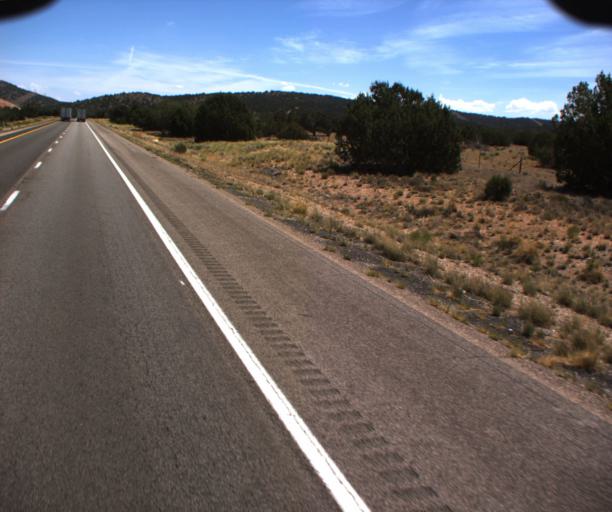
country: US
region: Arizona
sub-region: Mohave County
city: Peach Springs
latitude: 35.2745
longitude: -113.1367
